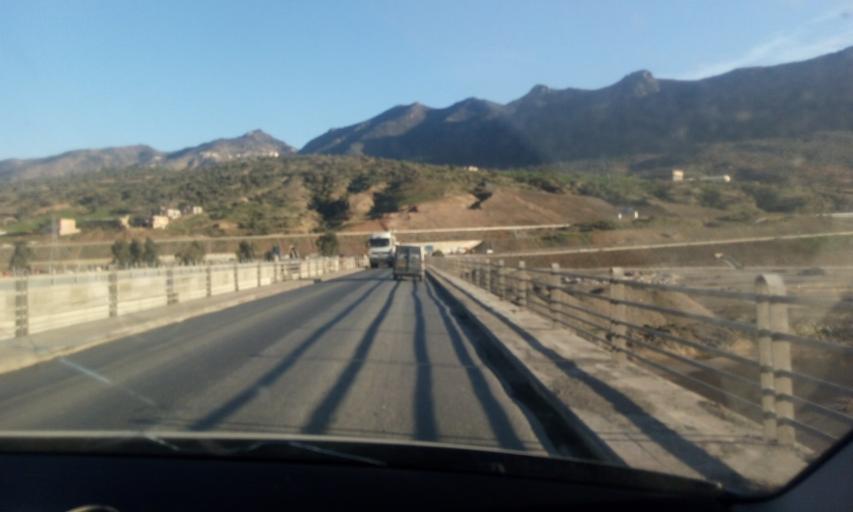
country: DZ
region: Bejaia
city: Akbou
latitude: 36.4818
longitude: 4.5912
